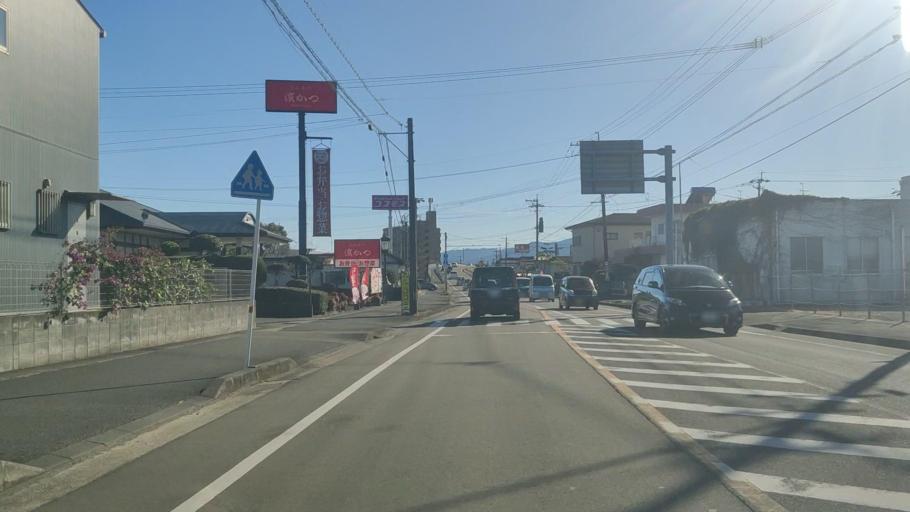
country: JP
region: Miyazaki
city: Miyazaki-shi
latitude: 31.8854
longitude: 131.4287
